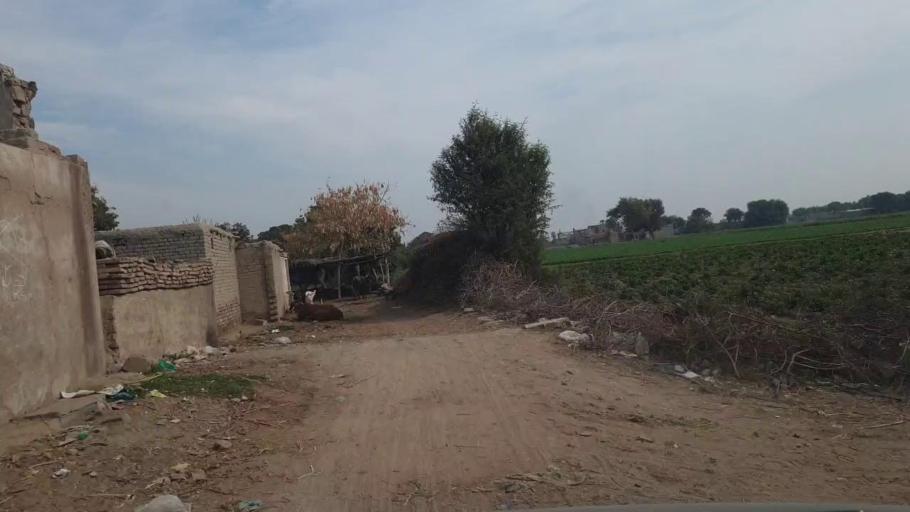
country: PK
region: Sindh
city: Shahdadpur
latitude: 25.9114
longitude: 68.6281
